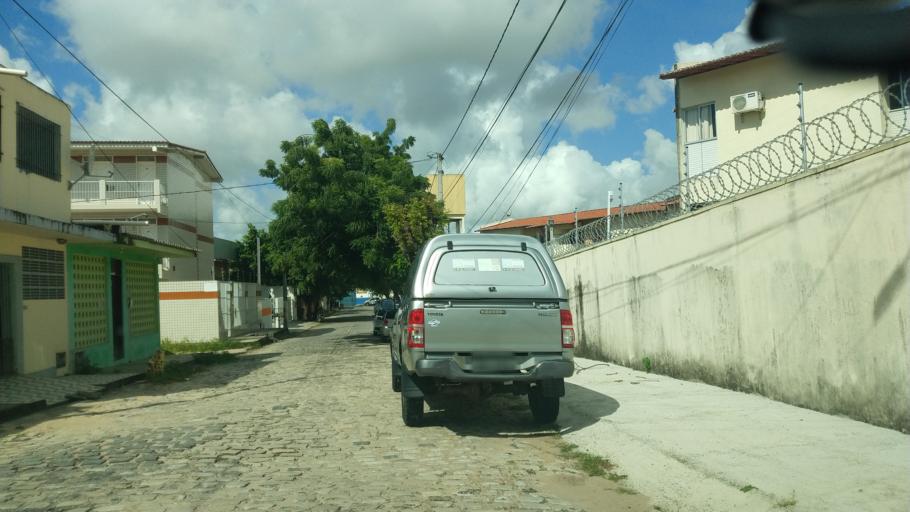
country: BR
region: Rio Grande do Norte
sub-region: Natal
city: Natal
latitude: -5.8596
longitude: -35.2082
